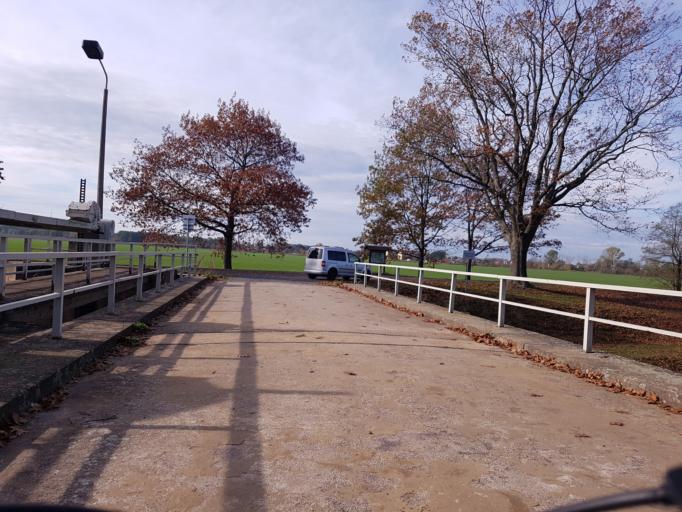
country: DE
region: Brandenburg
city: Schilda
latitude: 51.5985
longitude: 13.3235
